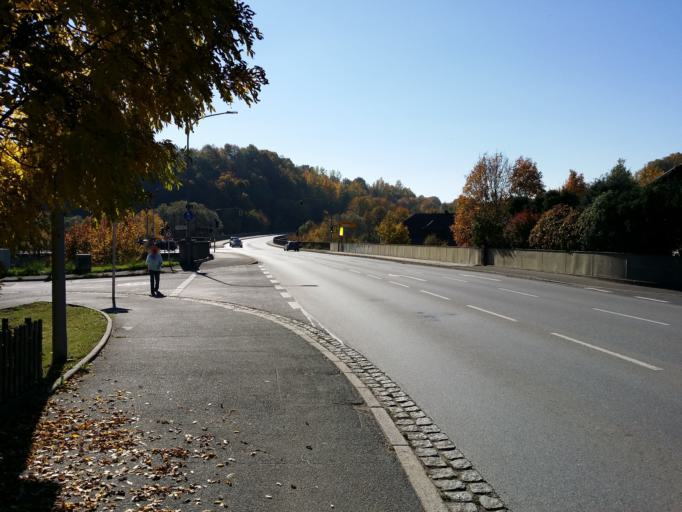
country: DE
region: Bavaria
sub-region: Upper Palatinate
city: Amberg
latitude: 49.4576
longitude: 11.8490
